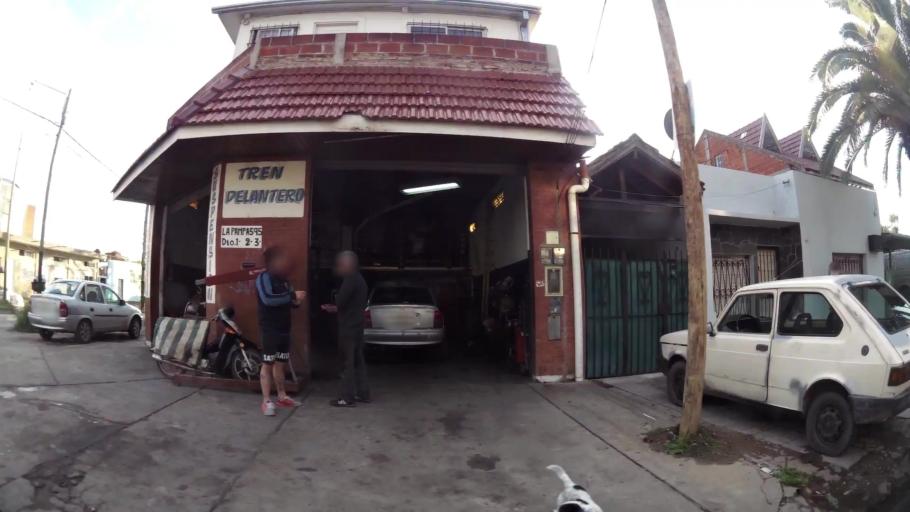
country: AR
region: Buenos Aires
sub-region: Partido de Almirante Brown
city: Adrogue
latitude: -34.7654
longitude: -58.3559
